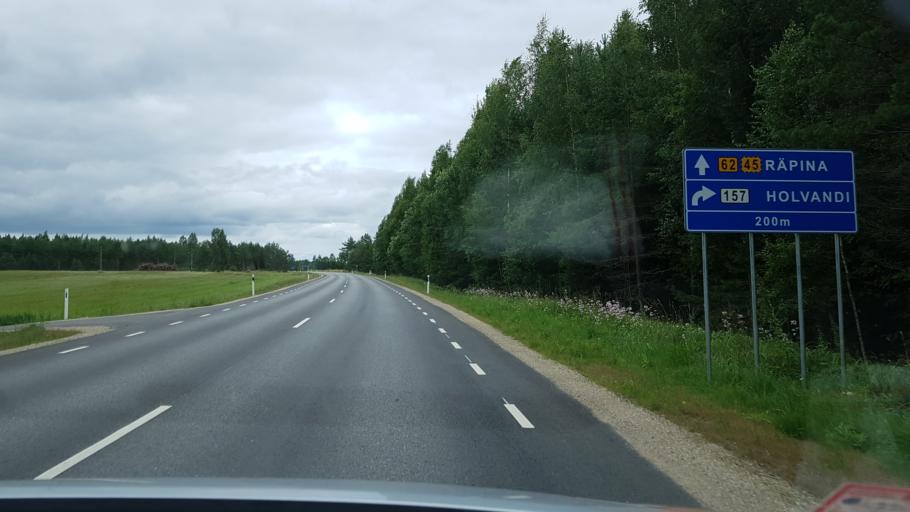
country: EE
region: Polvamaa
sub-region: Raepina vald
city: Rapina
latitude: 58.0720
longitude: 27.2675
